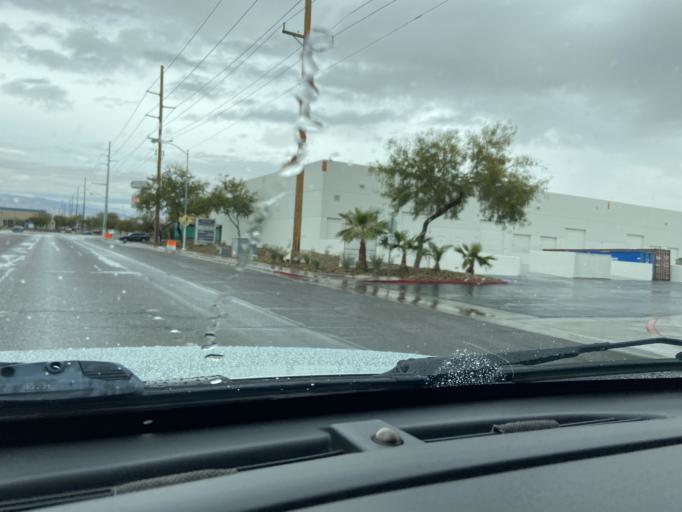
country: US
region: Nevada
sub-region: Clark County
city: Sunrise Manor
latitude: 36.2359
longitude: -115.0987
